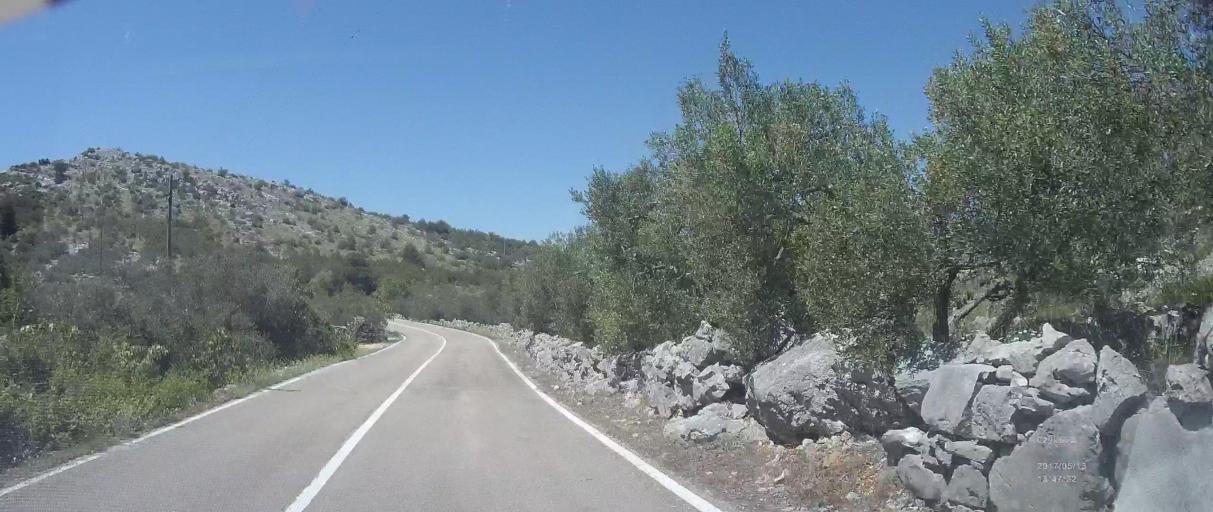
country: HR
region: Sibensko-Kniniska
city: Primosten
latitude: 43.6124
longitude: 15.9773
